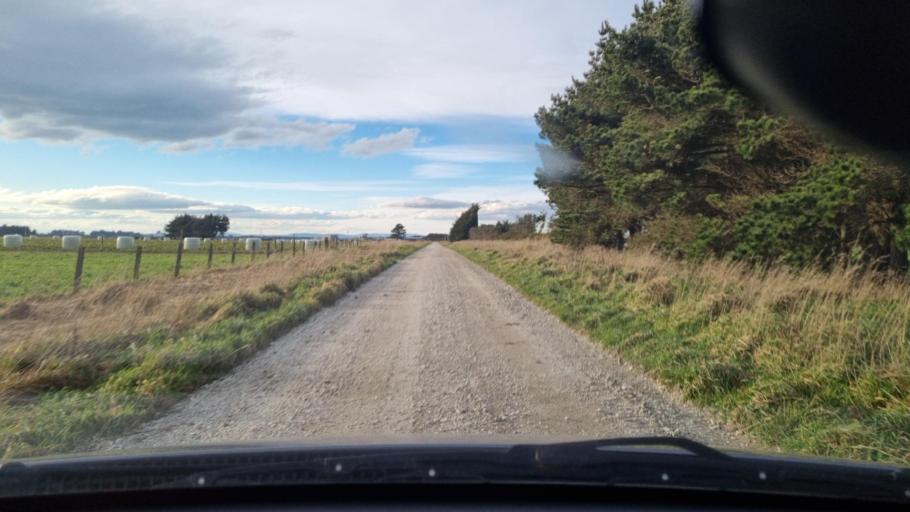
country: NZ
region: Southland
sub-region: Invercargill City
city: Invercargill
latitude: -46.3740
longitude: 168.2756
